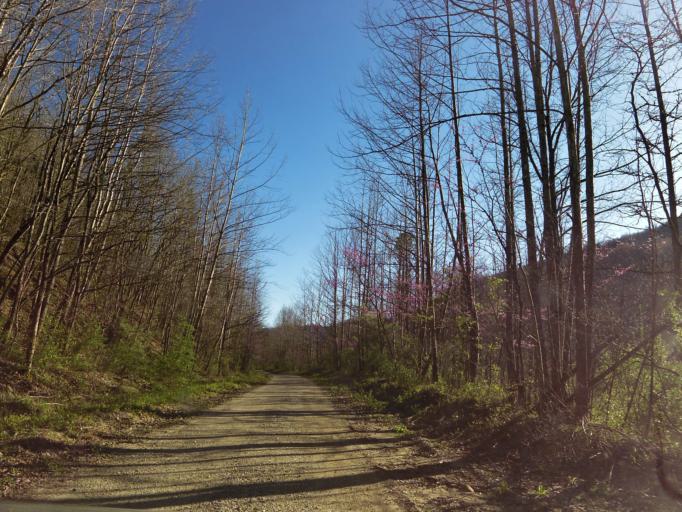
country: US
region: Tennessee
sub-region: Roane County
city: Oliver Springs
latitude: 36.2135
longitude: -84.4149
